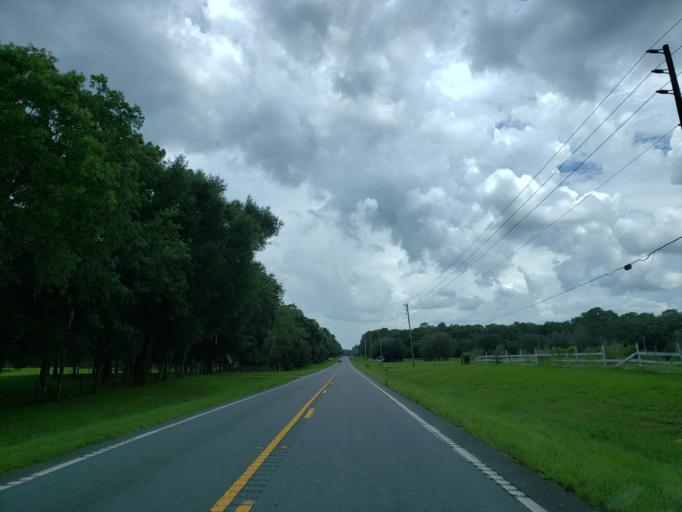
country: US
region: Florida
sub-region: Sumter County
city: Bushnell
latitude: 28.6401
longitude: -82.2268
